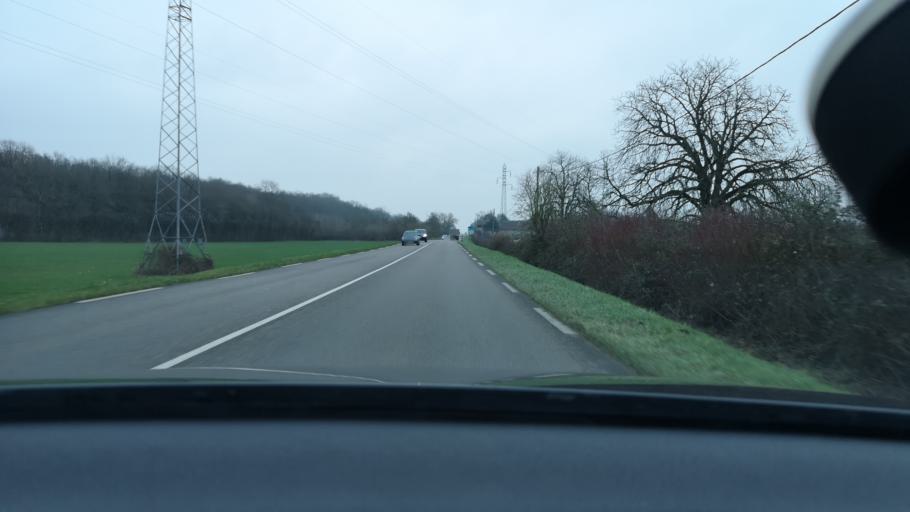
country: FR
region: Bourgogne
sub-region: Departement de Saone-et-Loire
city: Dracy-le-Fort
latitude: 46.8031
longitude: 4.7779
